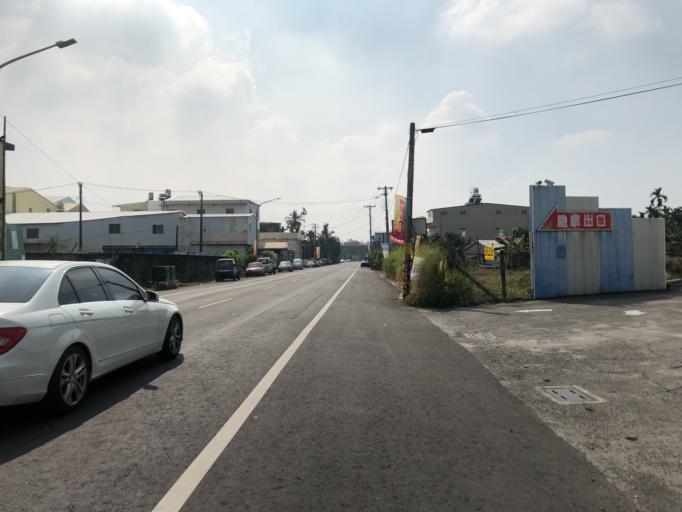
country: TW
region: Taiwan
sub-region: Pingtung
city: Pingtung
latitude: 22.5501
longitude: 120.5341
